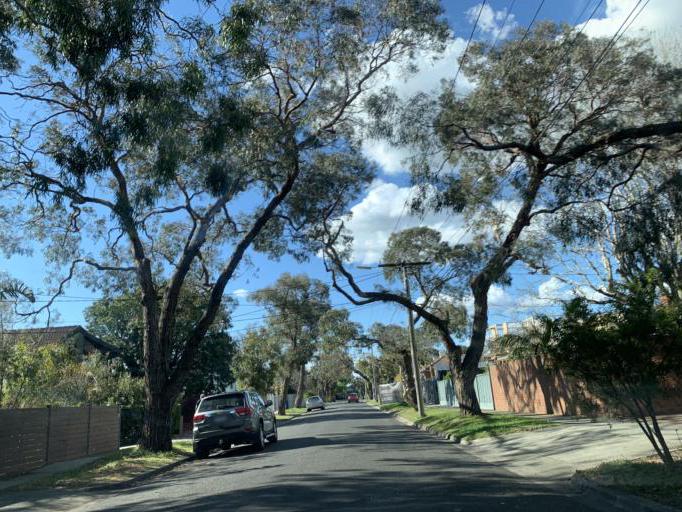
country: AU
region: Victoria
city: Hampton
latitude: -37.9509
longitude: 145.0123
